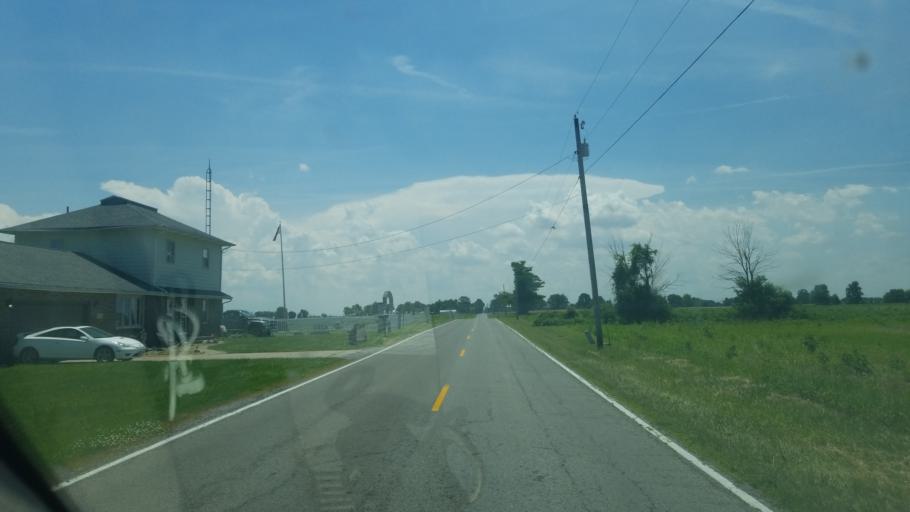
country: US
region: Ohio
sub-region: Hancock County
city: Arlington
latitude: 40.9432
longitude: -83.5942
